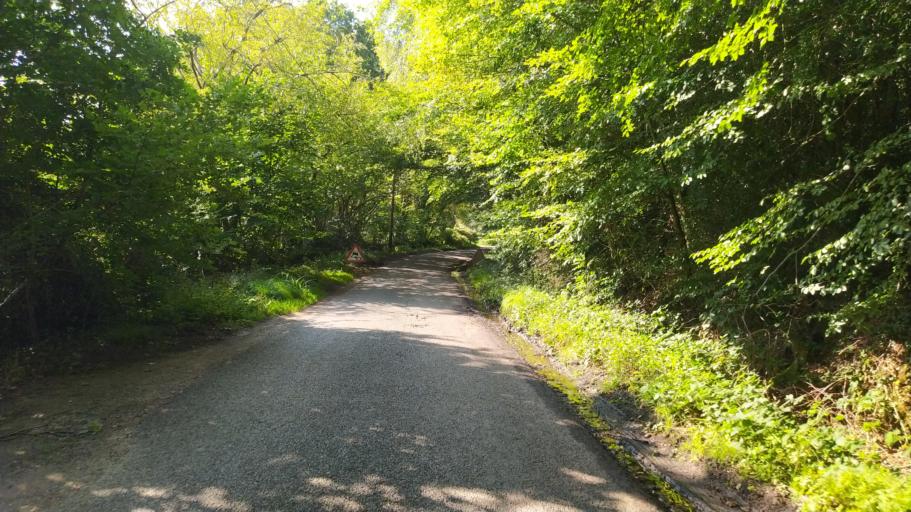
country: GB
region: England
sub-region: Hampshire
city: Lyndhurst
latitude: 50.8660
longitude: -1.5823
